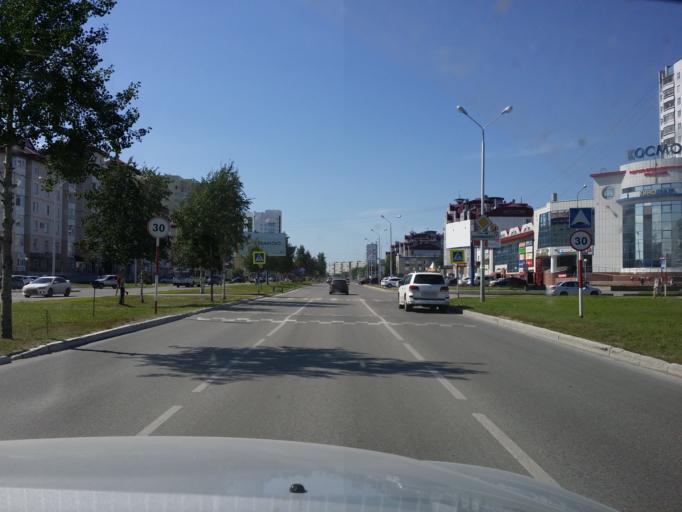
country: RU
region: Khanty-Mansiyskiy Avtonomnyy Okrug
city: Nizhnevartovsk
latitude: 60.9358
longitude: 76.5865
